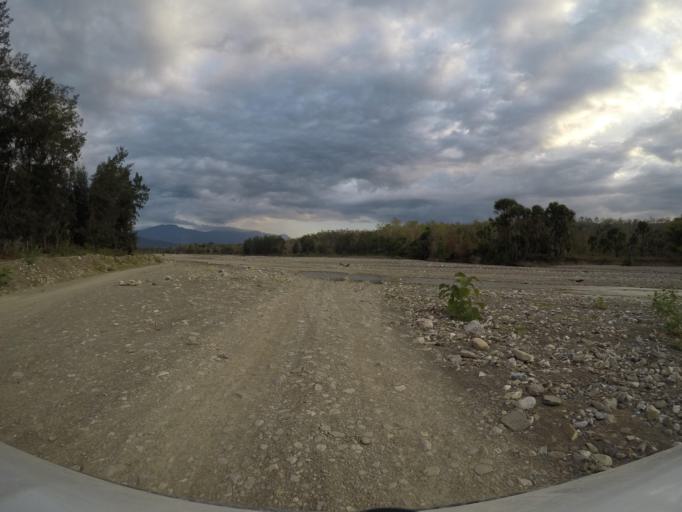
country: TL
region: Bobonaro
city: Maliana
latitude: -8.9026
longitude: 125.2092
